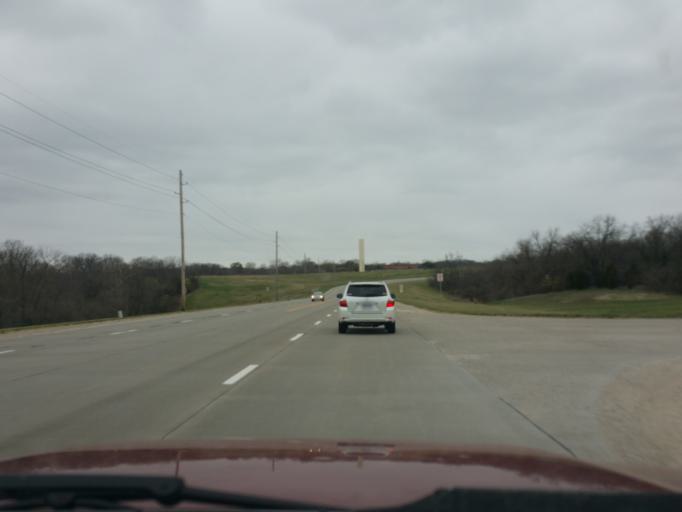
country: US
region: Kansas
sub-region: Wyandotte County
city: Edwardsville
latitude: 39.1092
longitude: -94.8435
